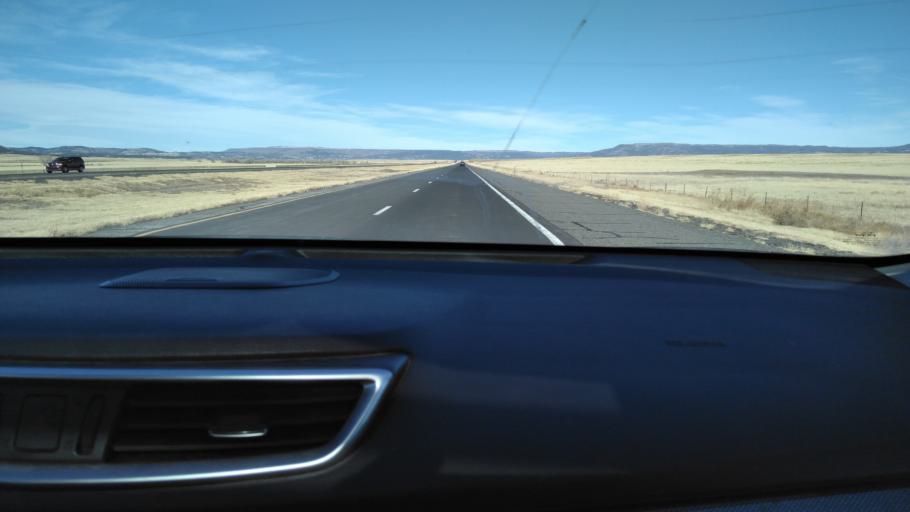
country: US
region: New Mexico
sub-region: Colfax County
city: Raton
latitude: 36.7332
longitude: -104.4573
